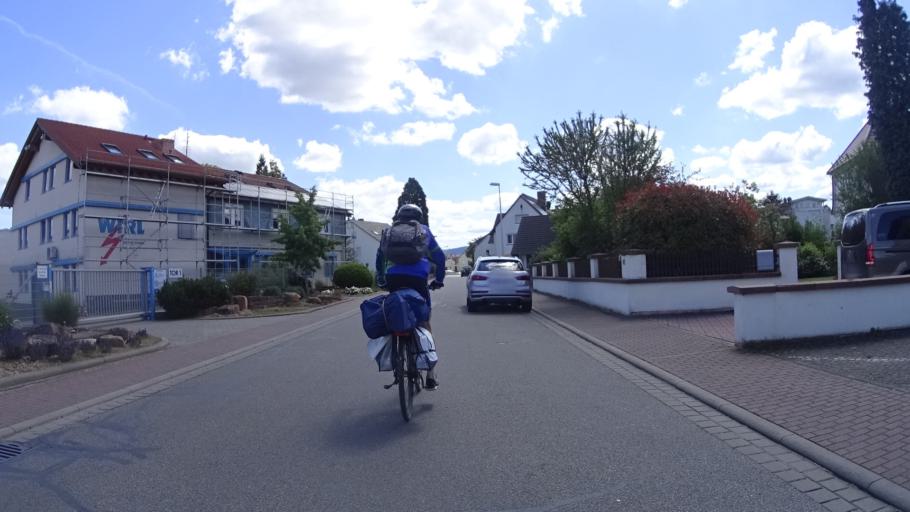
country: DE
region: Bavaria
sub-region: Regierungsbezirk Unterfranken
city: Kleinheubach
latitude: 49.7228
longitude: 9.2106
